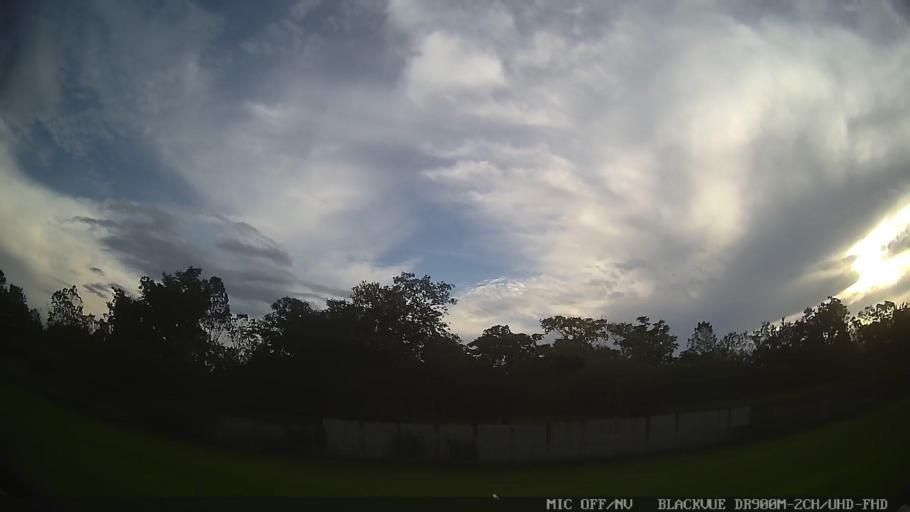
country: BR
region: Sao Paulo
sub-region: Porto Feliz
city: Porto Feliz
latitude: -23.2121
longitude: -47.5775
